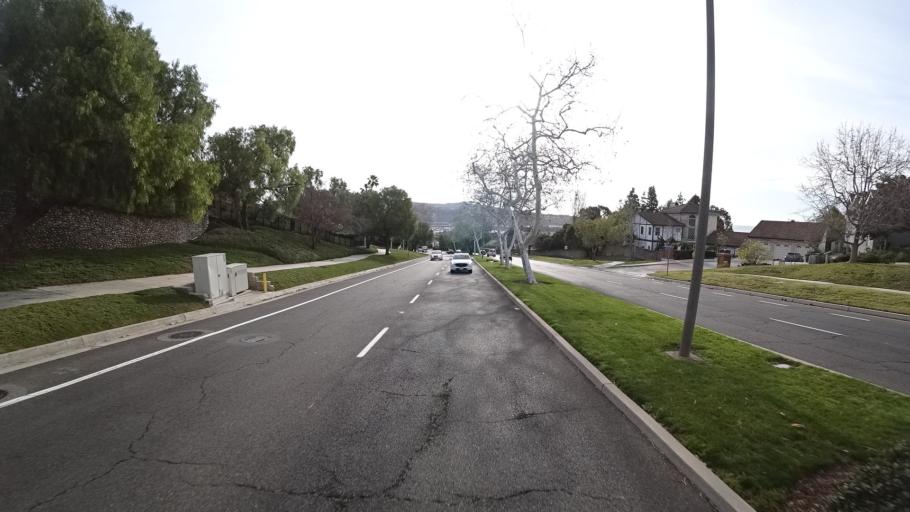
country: US
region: California
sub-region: Orange County
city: Dana Point
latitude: 33.4881
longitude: -117.6893
